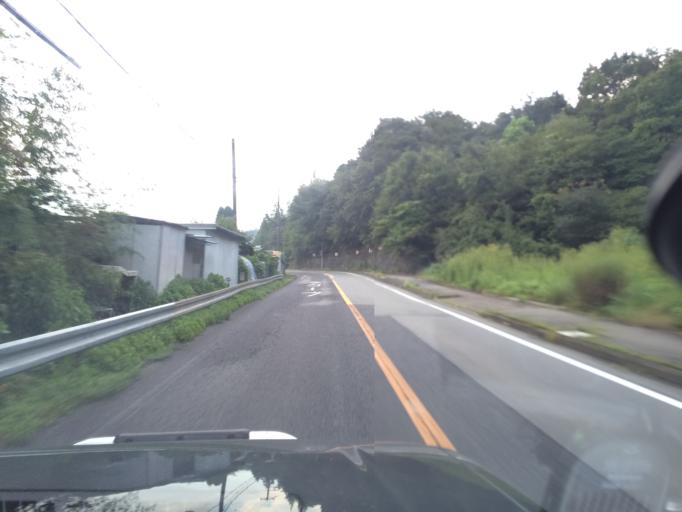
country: JP
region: Hyogo
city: Nishiwaki
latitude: 35.0979
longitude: 134.9968
